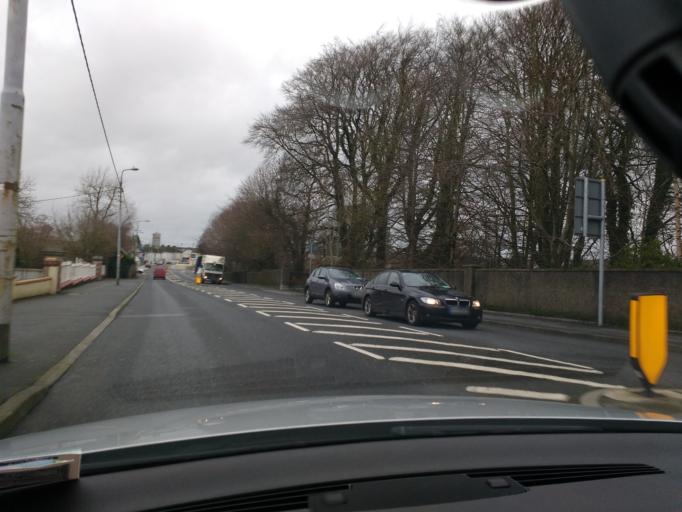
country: IE
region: Munster
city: Thurles
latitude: 52.6795
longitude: -7.7986
